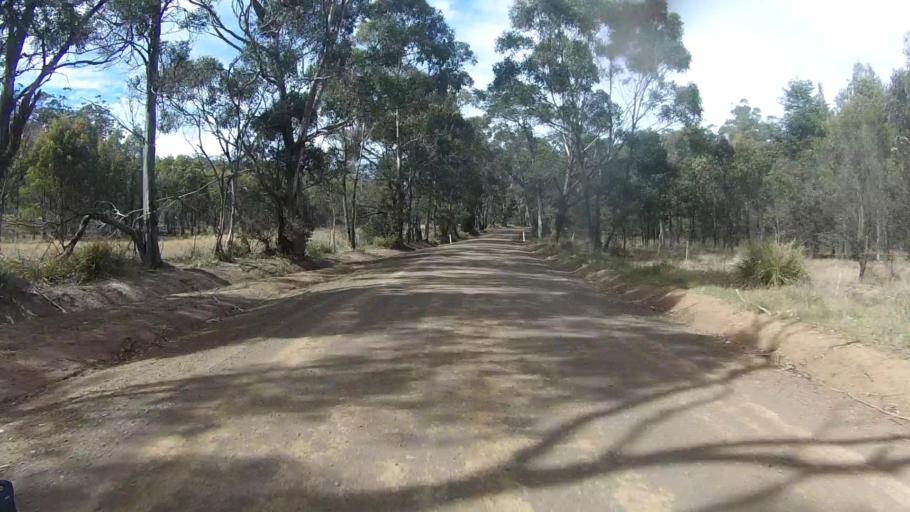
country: AU
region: Tasmania
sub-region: Sorell
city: Sorell
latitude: -42.6565
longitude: 147.8982
